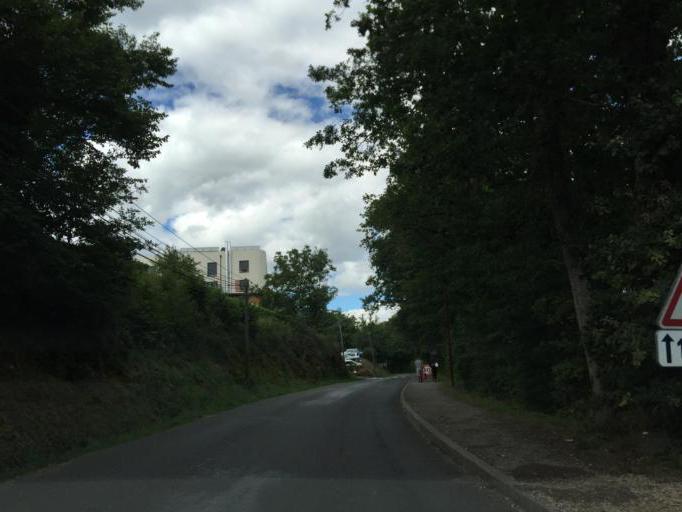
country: FR
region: Midi-Pyrenees
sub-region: Departement de l'Aveyron
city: Pont-de-Salars
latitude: 44.2844
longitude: 2.7262
